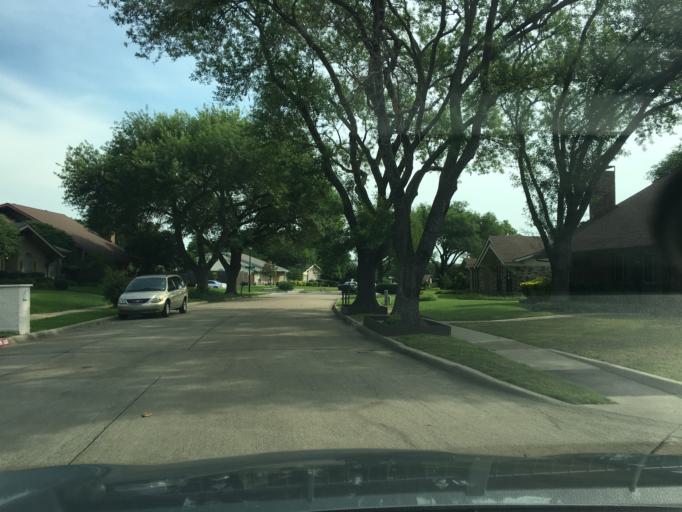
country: US
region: Texas
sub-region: Dallas County
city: Richardson
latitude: 32.9650
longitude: -96.6795
